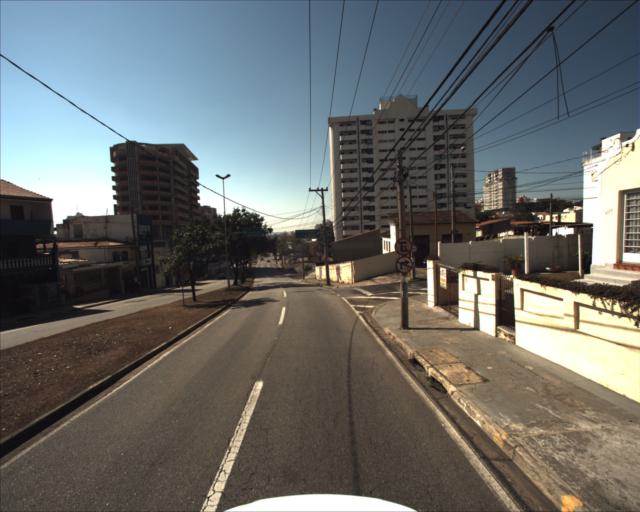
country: BR
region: Sao Paulo
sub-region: Sorocaba
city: Sorocaba
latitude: -23.4990
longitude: -47.4718
